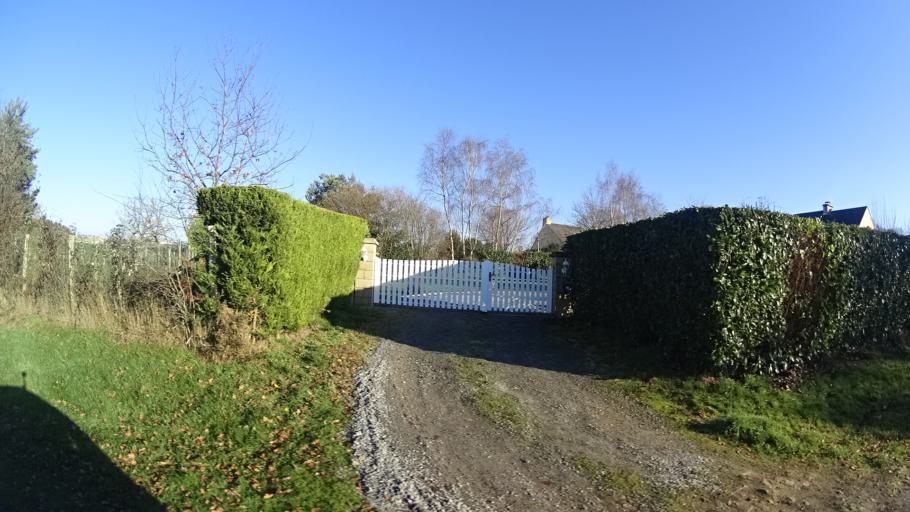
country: FR
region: Brittany
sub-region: Departement du Morbihan
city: Allaire
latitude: 47.6559
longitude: -2.1806
